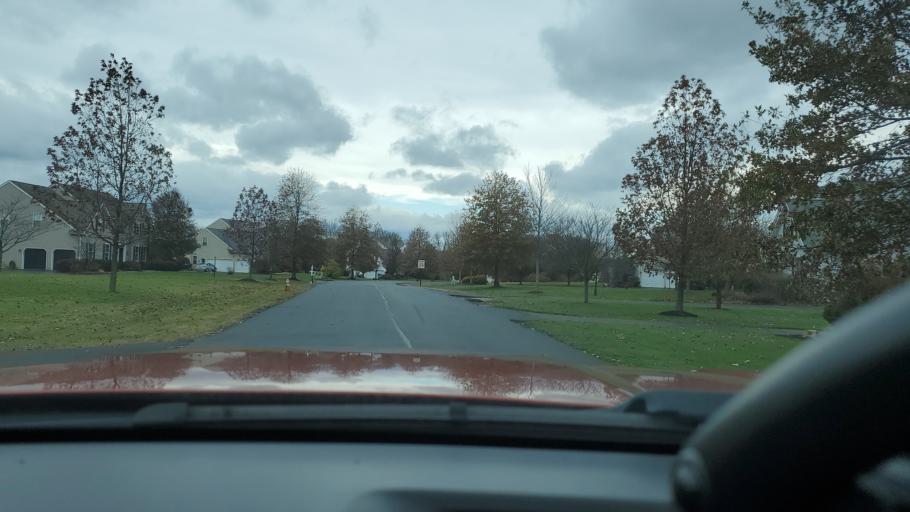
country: US
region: Pennsylvania
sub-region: Montgomery County
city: Spring Mount
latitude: 40.2889
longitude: -75.5062
